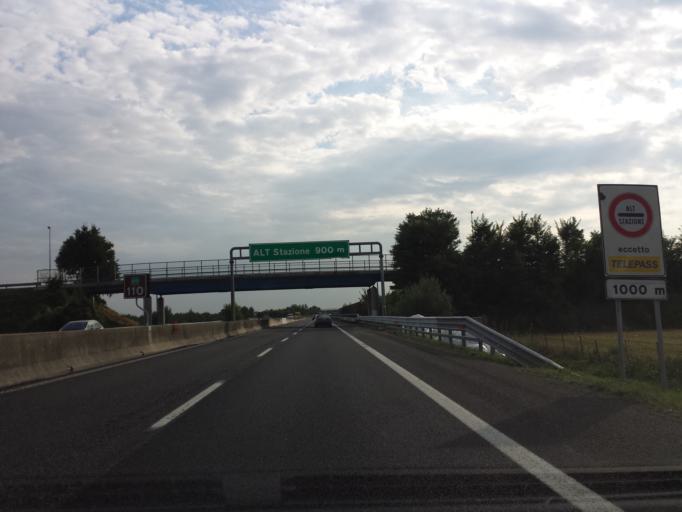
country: IT
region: Veneto
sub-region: Provincia di Padova
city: Mandriola-Sant'Agostino
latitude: 45.3538
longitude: 11.8539
